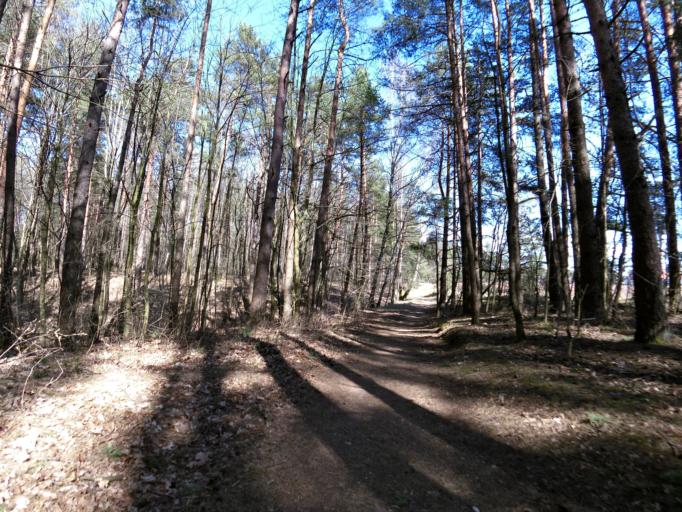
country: LT
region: Vilnius County
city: Pilaite
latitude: 54.6861
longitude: 25.1916
